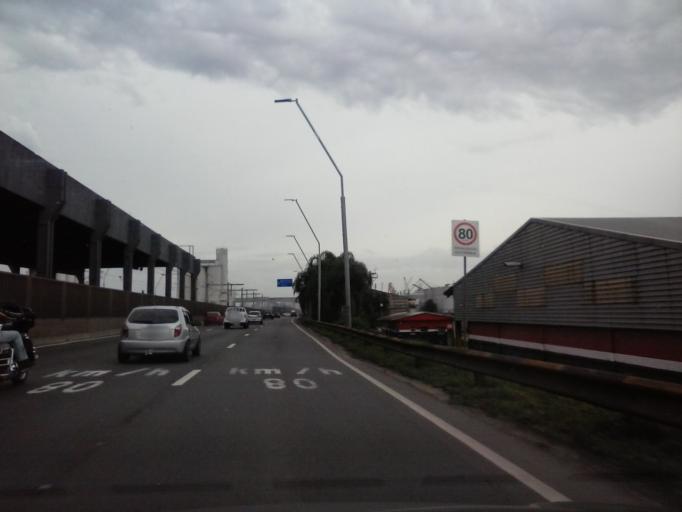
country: BR
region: Rio Grande do Sul
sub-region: Porto Alegre
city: Porto Alegre
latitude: -30.0063
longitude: -51.2096
